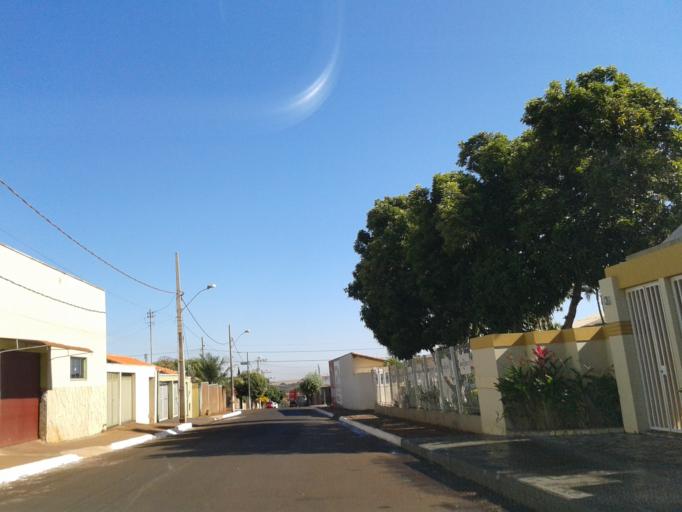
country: BR
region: Minas Gerais
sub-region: Capinopolis
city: Capinopolis
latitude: -18.6827
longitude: -49.5666
